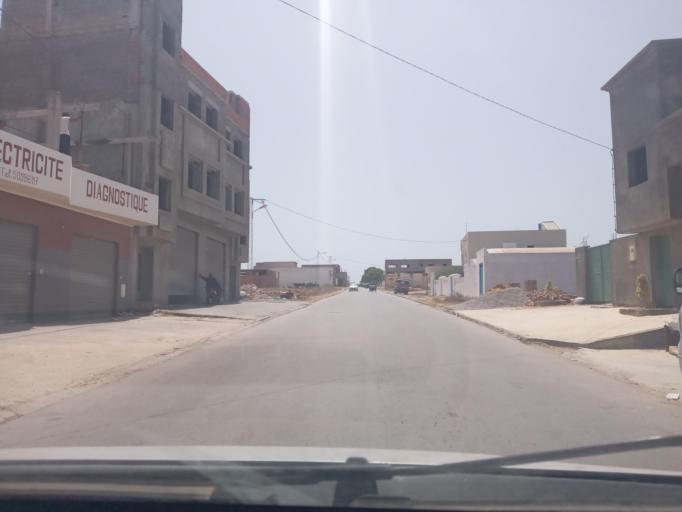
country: TN
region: Nabul
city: El Haouaria
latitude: 37.0445
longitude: 11.0236
